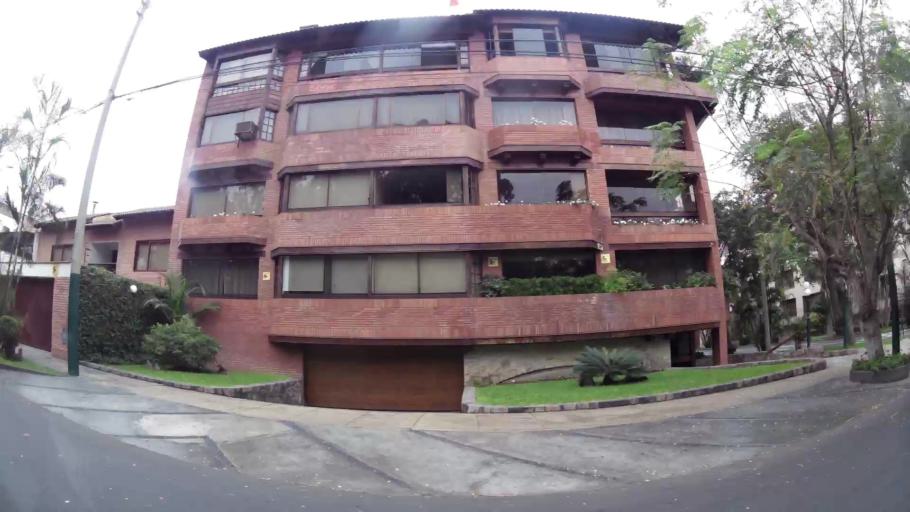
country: PE
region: Lima
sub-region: Lima
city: Surco
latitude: -12.1181
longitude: -76.9820
